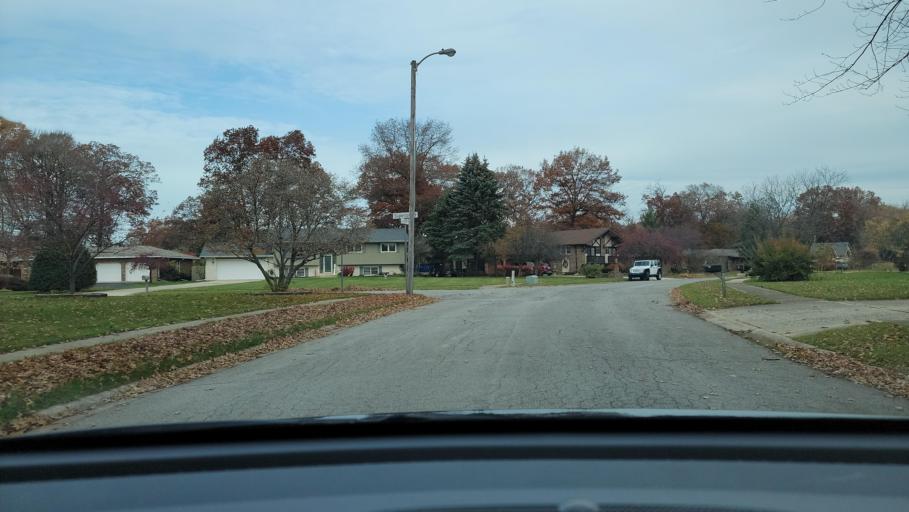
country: US
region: Indiana
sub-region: Porter County
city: Portage
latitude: 41.5828
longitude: -87.1478
